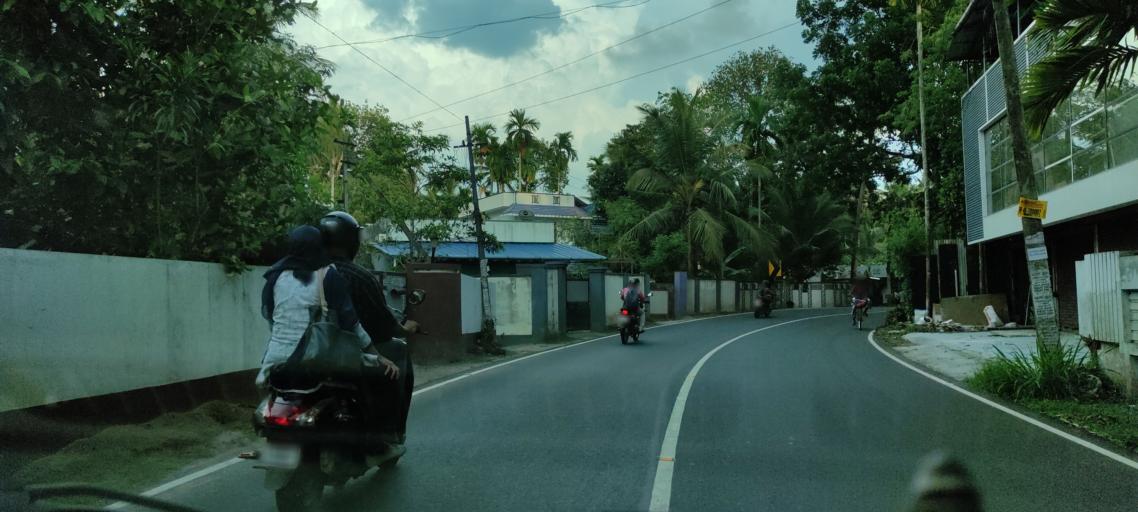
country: IN
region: Kerala
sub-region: Alappuzha
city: Arukutti
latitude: 9.8612
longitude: 76.3242
